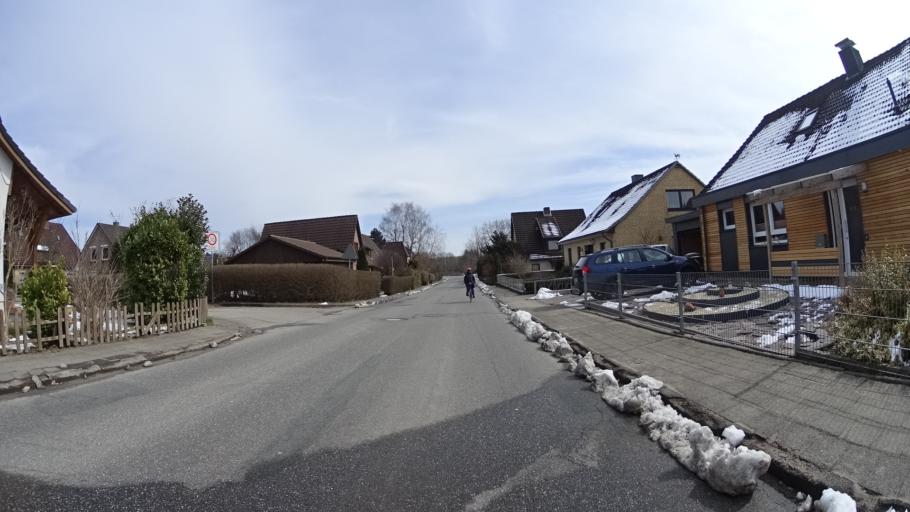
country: DE
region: Schleswig-Holstein
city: Wankendorf
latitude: 54.1112
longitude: 10.2114
